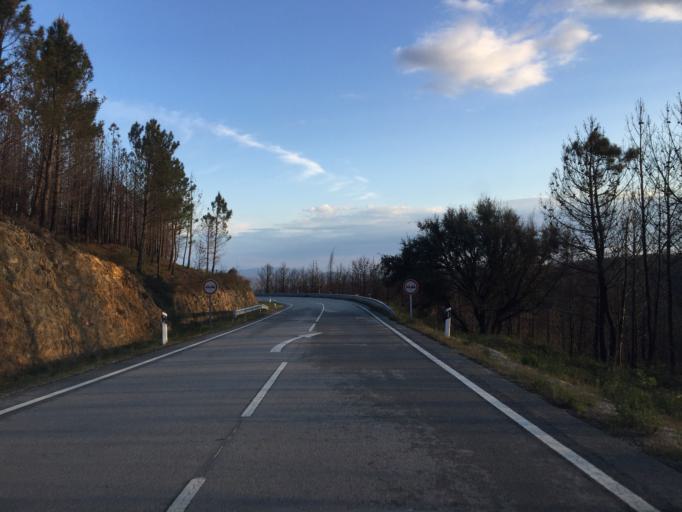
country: PT
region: Coimbra
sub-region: Pampilhosa da Serra
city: Pampilhosa da Serra
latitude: 40.1009
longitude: -7.9974
